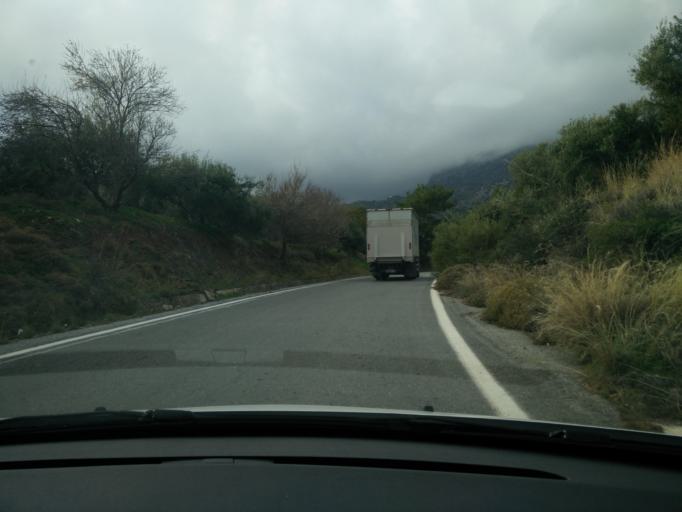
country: GR
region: Crete
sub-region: Nomos Lasithiou
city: Gra Liyia
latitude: 35.0214
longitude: 25.5739
